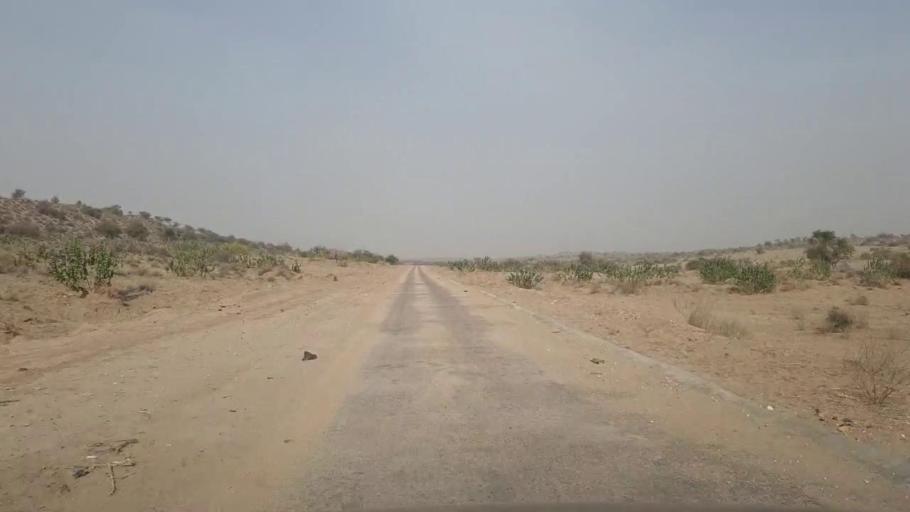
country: PK
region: Sindh
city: Chor
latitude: 25.6238
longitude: 69.9385
